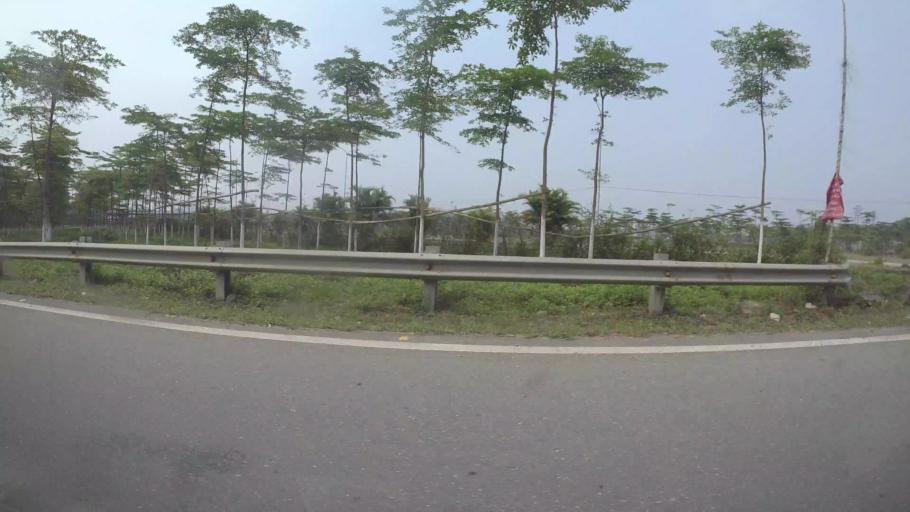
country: VN
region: Ha Noi
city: Lien Quan
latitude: 20.9933
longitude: 105.5243
